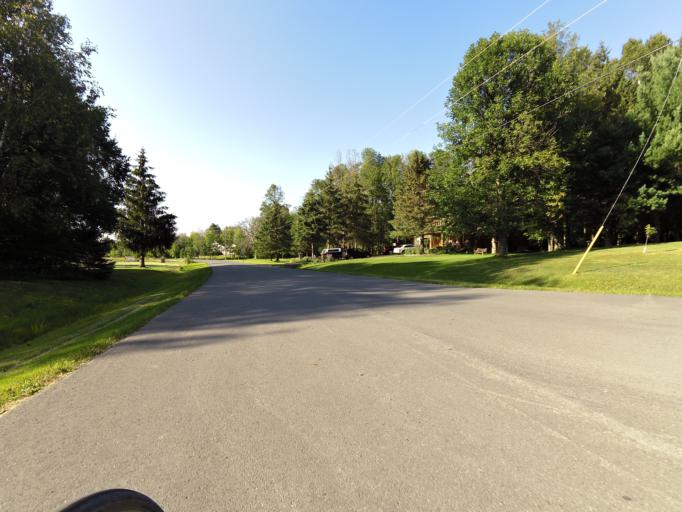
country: CA
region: Ontario
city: Bells Corners
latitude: 45.4763
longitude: -76.0315
